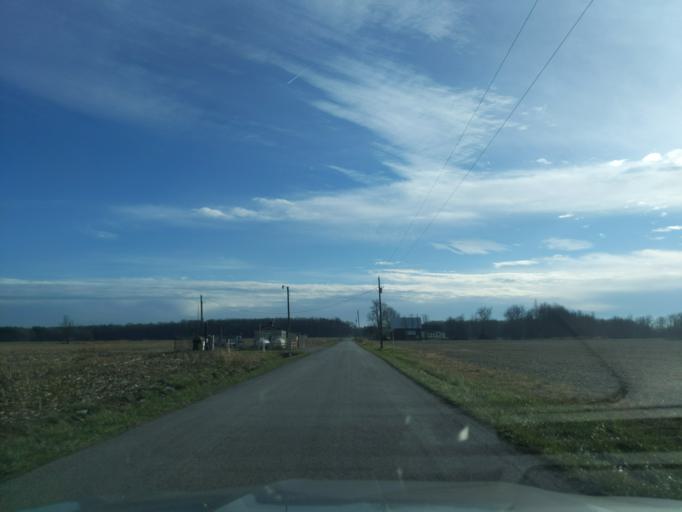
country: US
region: Indiana
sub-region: Decatur County
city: Westport
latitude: 39.1947
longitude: -85.4619
